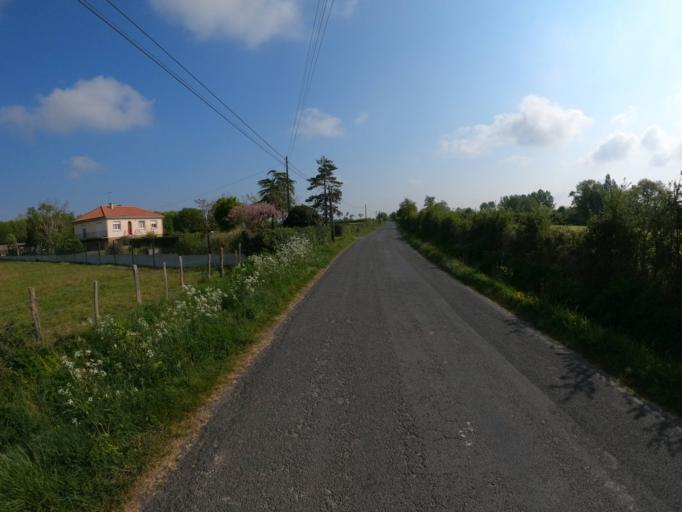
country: FR
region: Pays de la Loire
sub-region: Departement de Maine-et-Loire
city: Torfou
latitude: 47.0565
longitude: -1.0920
